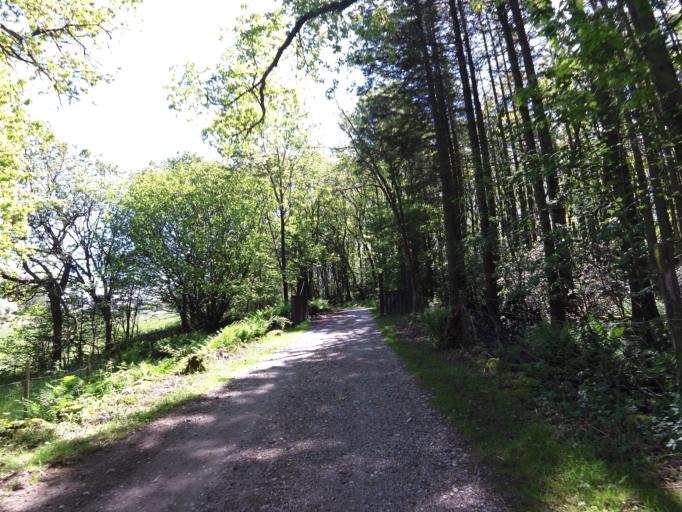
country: NO
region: Rogaland
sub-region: Eigersund
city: Egersund
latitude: 58.5025
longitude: 5.9100
